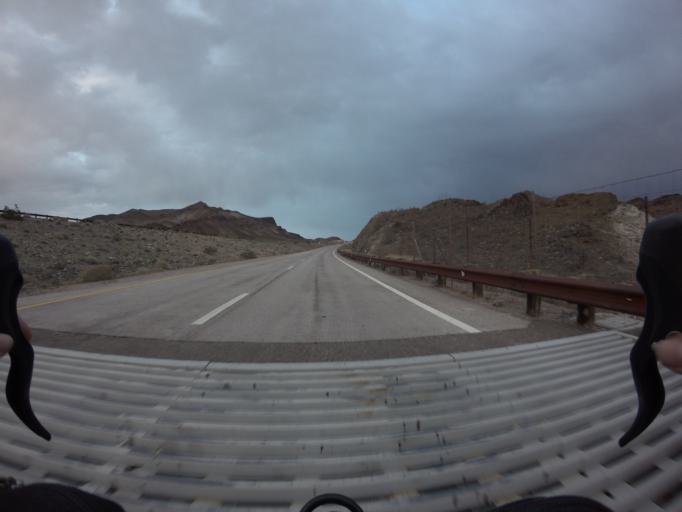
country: US
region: Nevada
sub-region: Clark County
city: Boulder City
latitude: 36.0016
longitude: -114.7229
